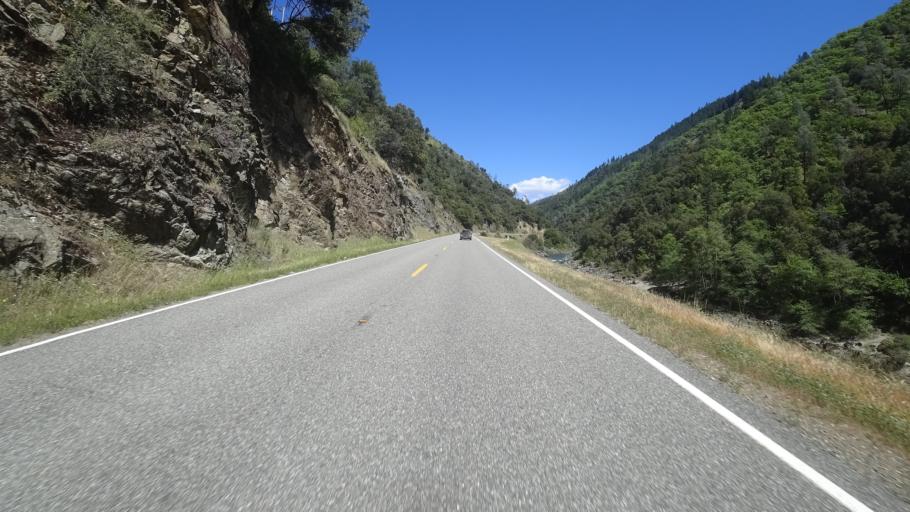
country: US
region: California
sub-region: Trinity County
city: Hayfork
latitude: 40.7430
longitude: -123.1826
